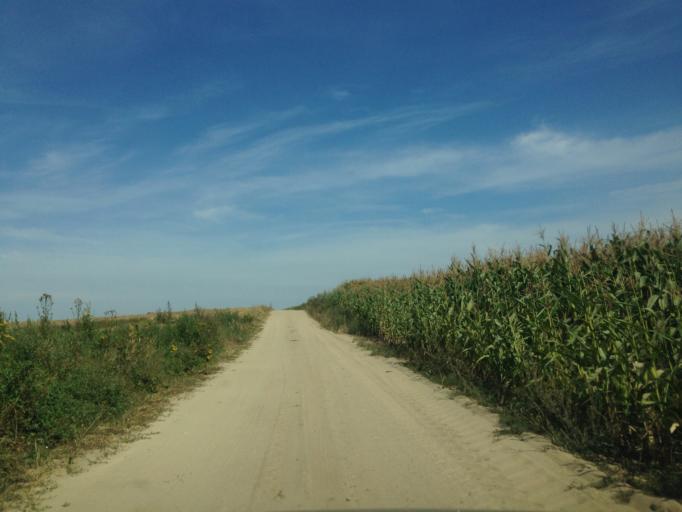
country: PL
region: Kujawsko-Pomorskie
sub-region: Powiat brodnicki
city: Bartniczka
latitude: 53.2240
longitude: 19.5505
